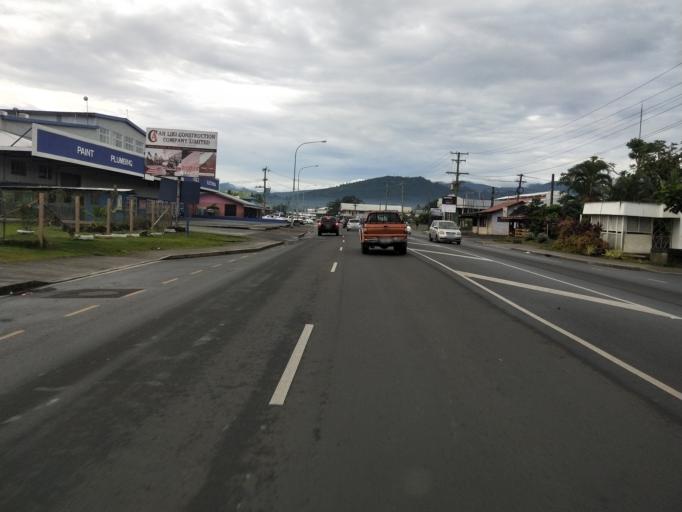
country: WS
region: Tuamasaga
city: Vaiusu
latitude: -13.8180
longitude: -171.8070
